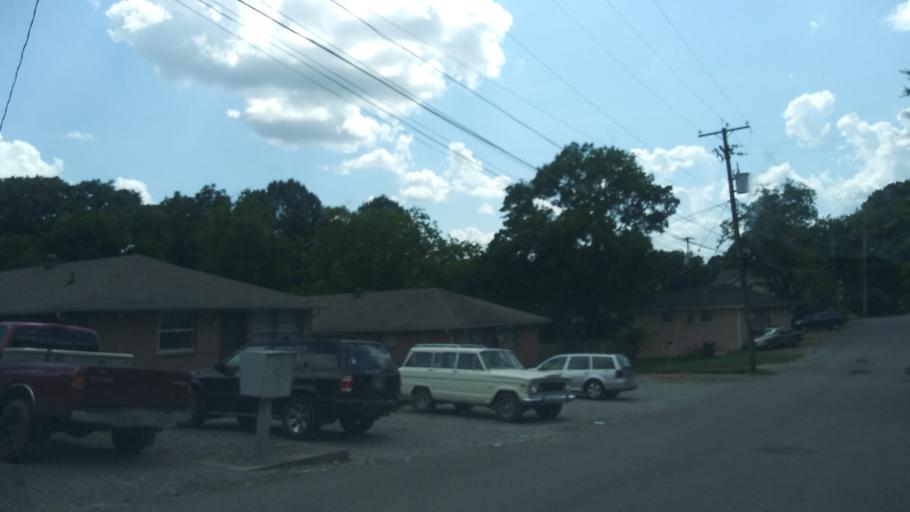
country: US
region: Tennessee
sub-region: Davidson County
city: Nashville
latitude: 36.1450
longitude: -86.8277
